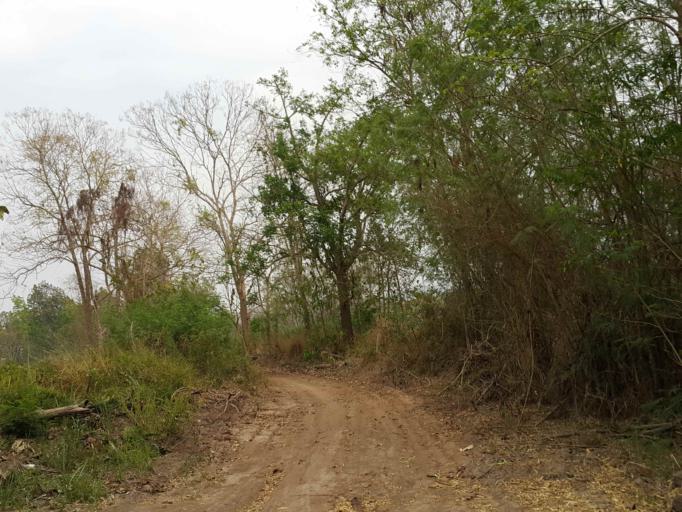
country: TH
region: Chiang Mai
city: Mae Taeng
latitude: 19.1148
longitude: 98.9885
